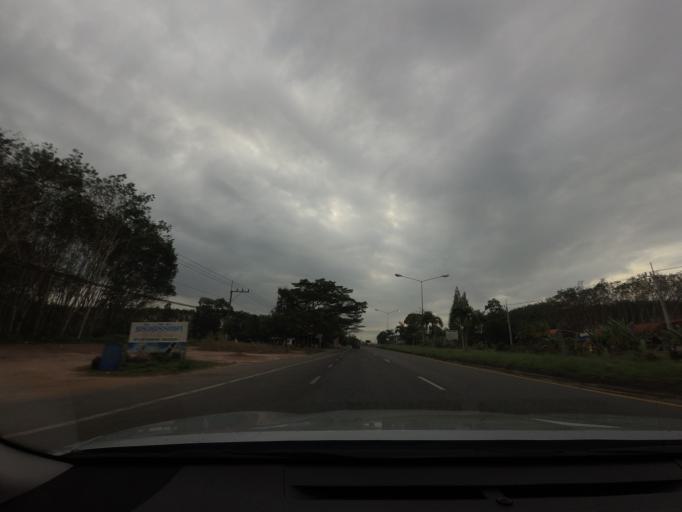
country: TH
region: Surat Thani
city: Phunphin
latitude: 9.0398
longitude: 99.1450
